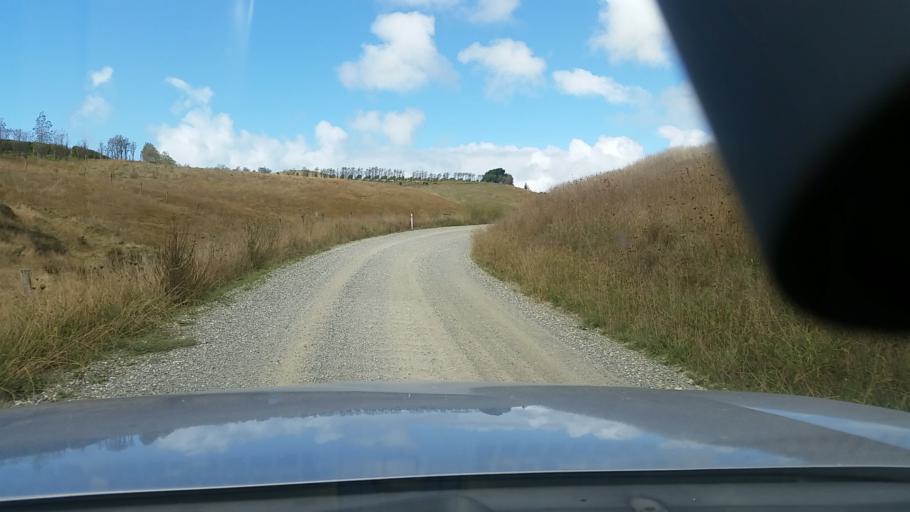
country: NZ
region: Marlborough
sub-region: Marlborough District
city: Blenheim
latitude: -41.6890
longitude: 174.1399
